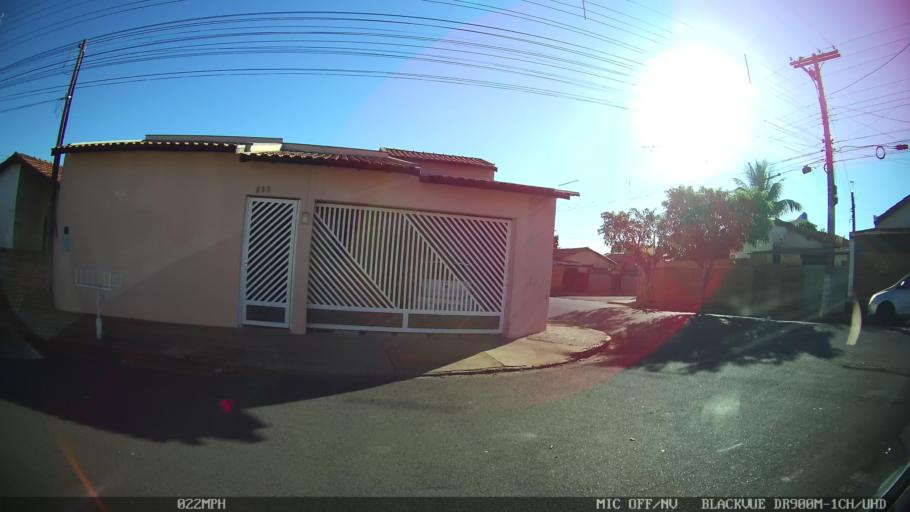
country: BR
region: Sao Paulo
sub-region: Olimpia
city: Olimpia
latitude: -20.7286
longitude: -48.9090
